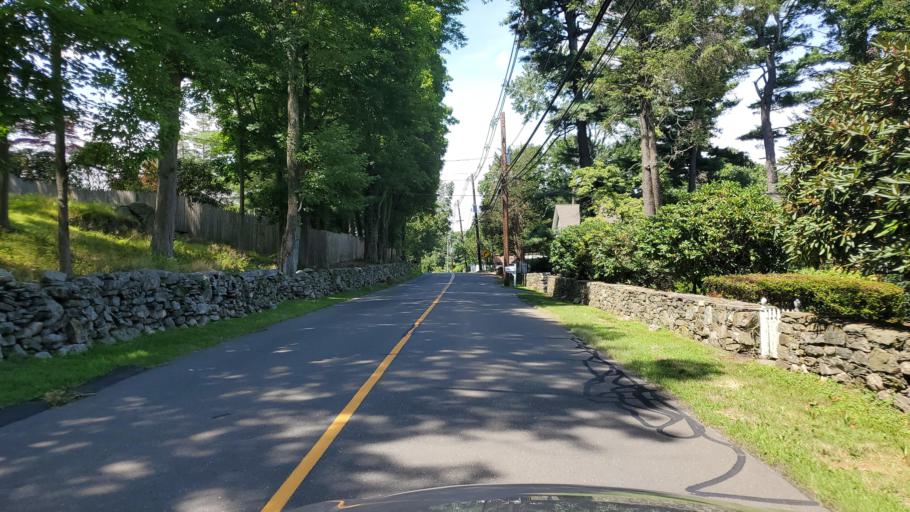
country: US
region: Connecticut
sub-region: Fairfield County
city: Westport
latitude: 41.1290
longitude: -73.3298
